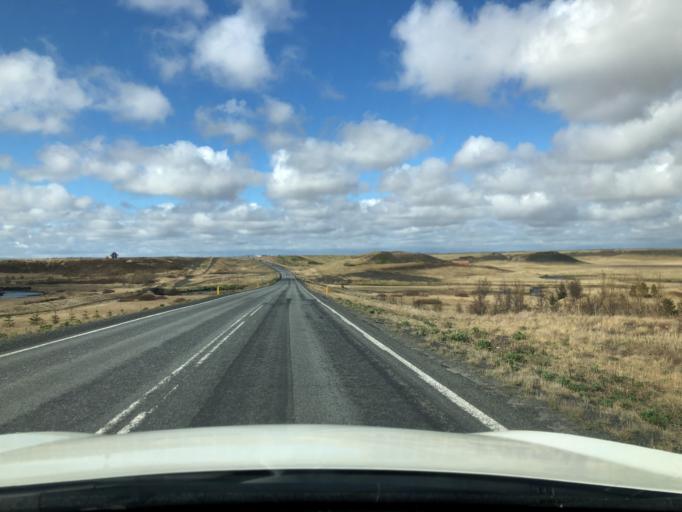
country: IS
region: South
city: Vestmannaeyjar
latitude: 63.8181
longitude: -20.3529
